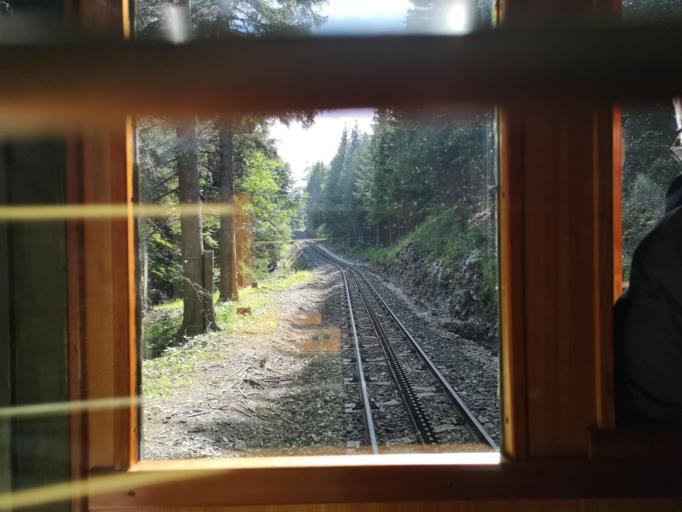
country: AT
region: Lower Austria
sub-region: Politischer Bezirk Neunkirchen
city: Puchberg am Schneeberg
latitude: 47.7540
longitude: 15.8732
